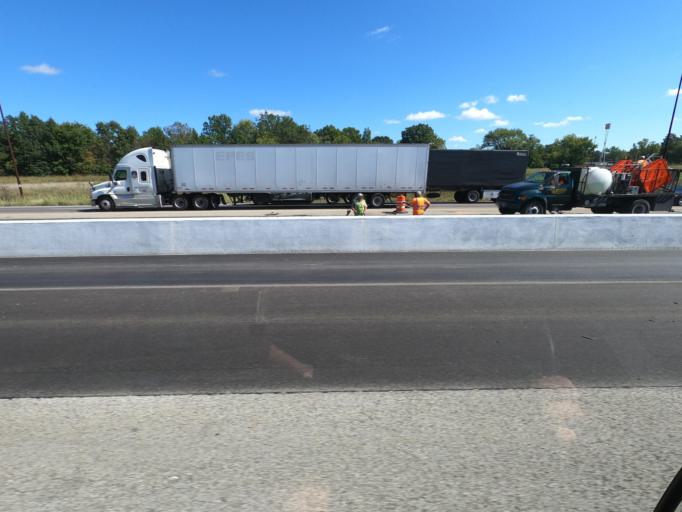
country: US
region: Illinois
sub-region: Franklin County
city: West Frankfort
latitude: 37.8989
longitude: -88.9470
